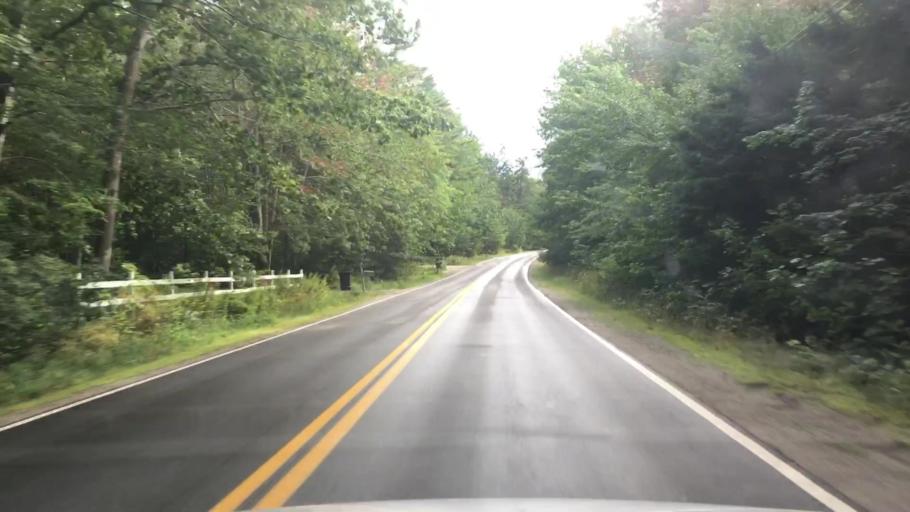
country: US
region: Maine
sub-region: Hancock County
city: Trenton
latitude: 44.4625
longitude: -68.4242
